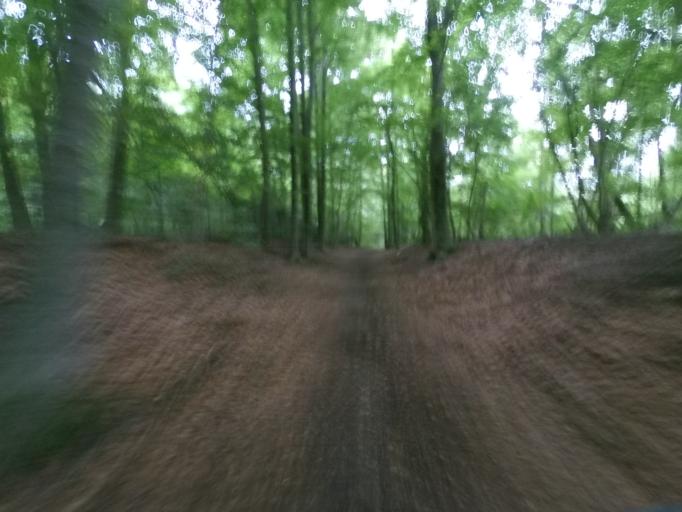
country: DE
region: Schleswig-Holstein
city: Oststeinbek
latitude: 53.5061
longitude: 10.1736
